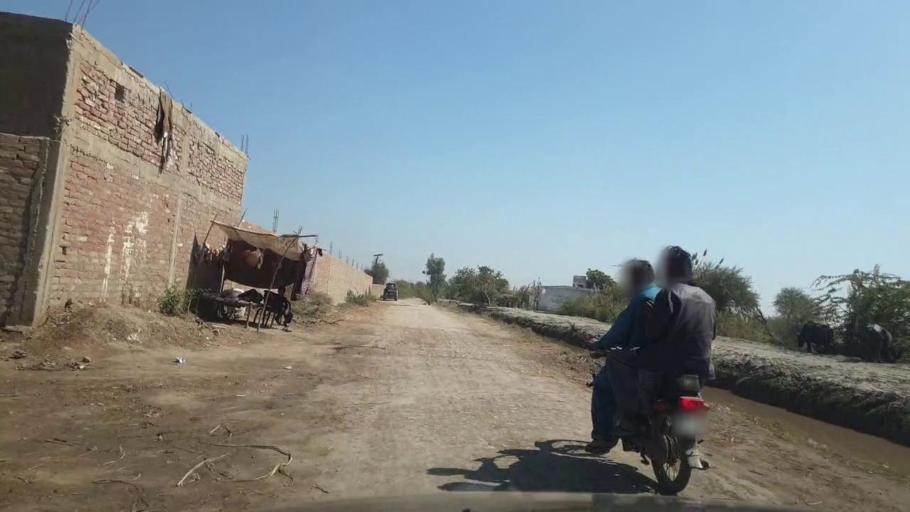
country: PK
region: Sindh
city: Mirpur Khas
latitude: 25.5709
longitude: 69.0704
